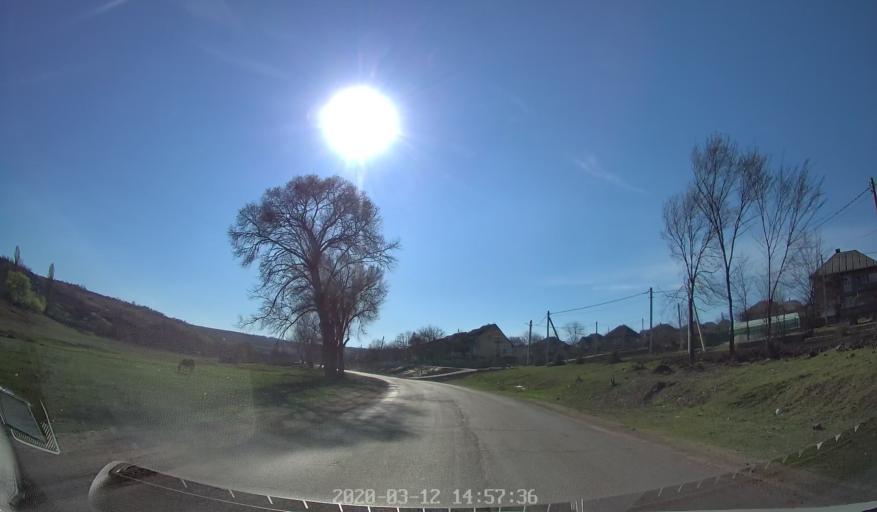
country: MD
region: Telenesti
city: Cocieri
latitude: 47.2230
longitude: 29.0362
